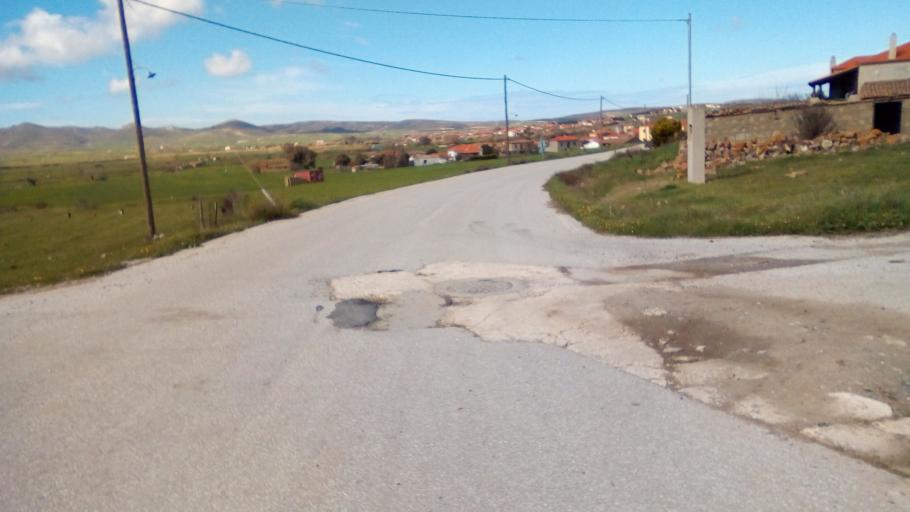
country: GR
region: North Aegean
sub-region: Nomos Lesvou
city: Myrina
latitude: 39.9307
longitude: 25.2312
